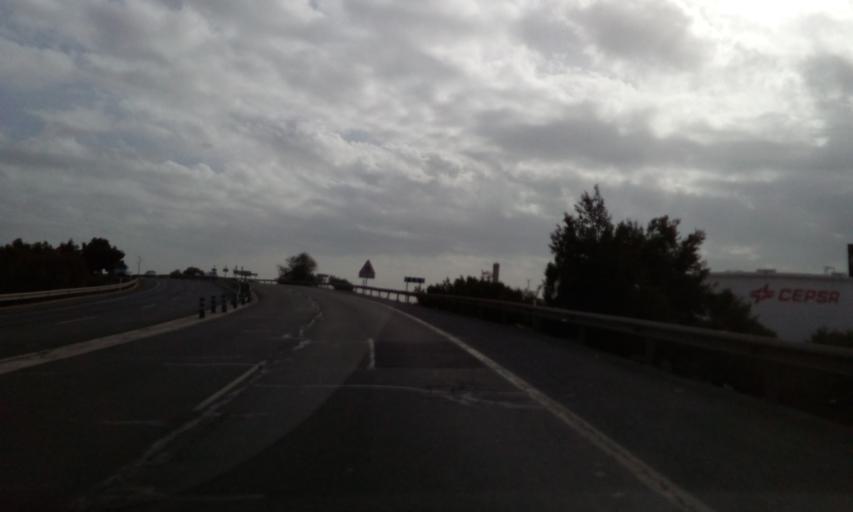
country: ES
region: Andalusia
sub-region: Provincia de Huelva
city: Punta Umbria
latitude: 37.2036
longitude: -6.9363
